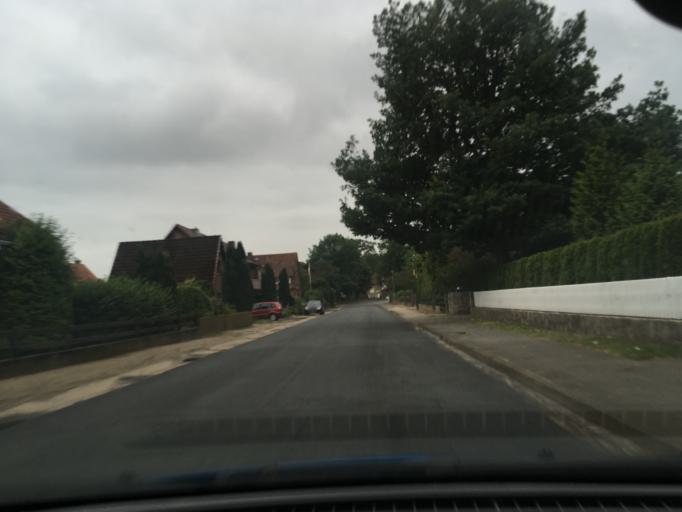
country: DE
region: Lower Saxony
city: Egestorf
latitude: 53.1964
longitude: 10.0641
